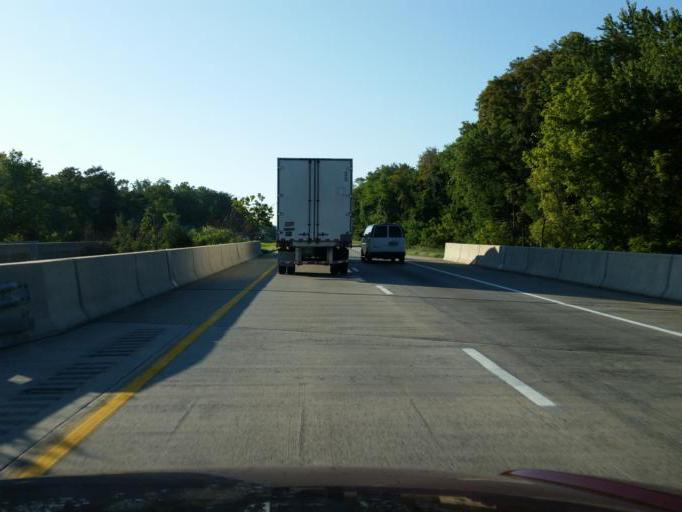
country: US
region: Pennsylvania
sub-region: Dauphin County
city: Middletown
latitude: 40.2002
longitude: -76.6996
